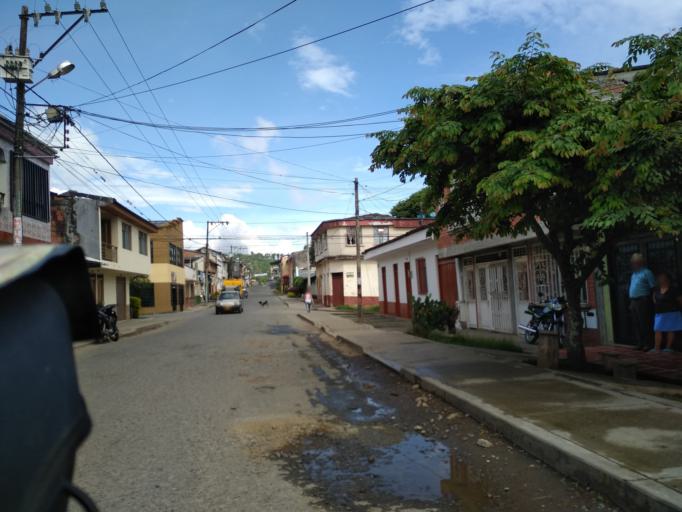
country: CO
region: Valle del Cauca
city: Caicedonia
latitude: 4.3304
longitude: -75.8265
